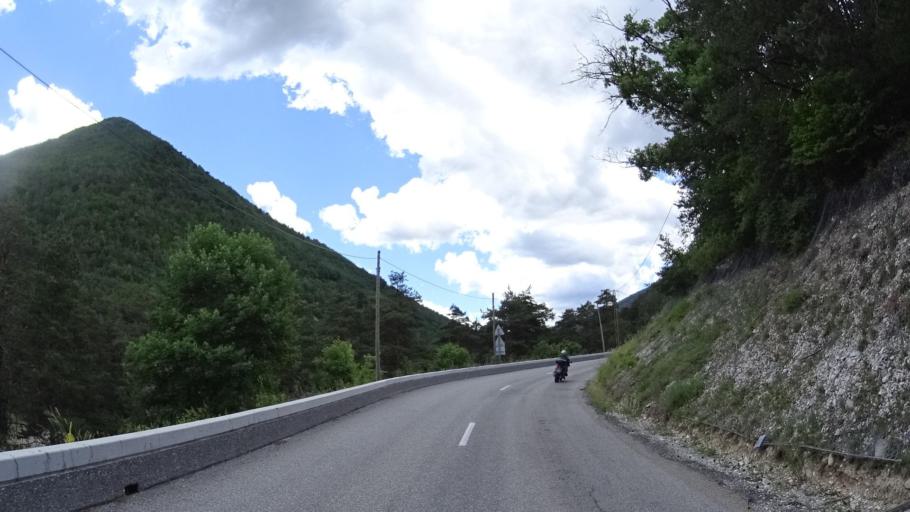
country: FR
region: Provence-Alpes-Cote d'Azur
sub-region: Departement des Alpes-de-Haute-Provence
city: Annot
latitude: 44.0370
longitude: 6.5620
